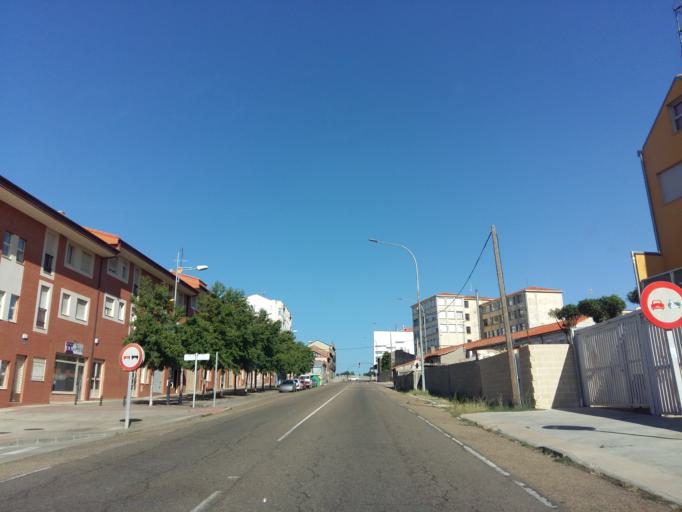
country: ES
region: Castille and Leon
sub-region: Provincia de Leon
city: Astorga
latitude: 42.4544
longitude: -6.0586
